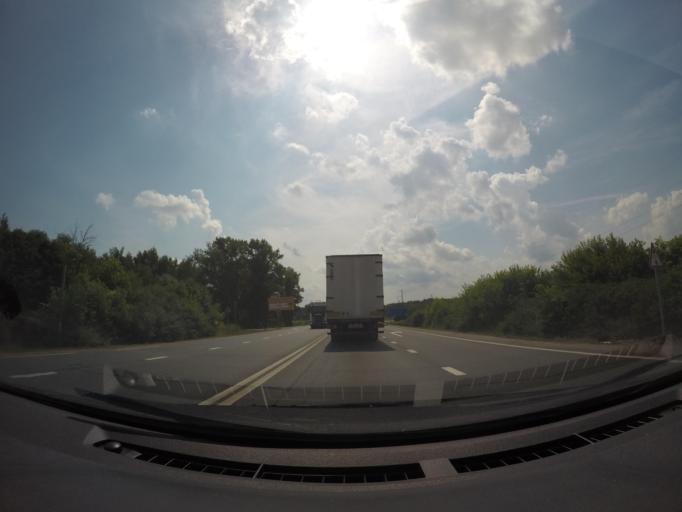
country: RU
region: Moskovskaya
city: Malyshevo
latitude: 55.4858
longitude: 38.3436
